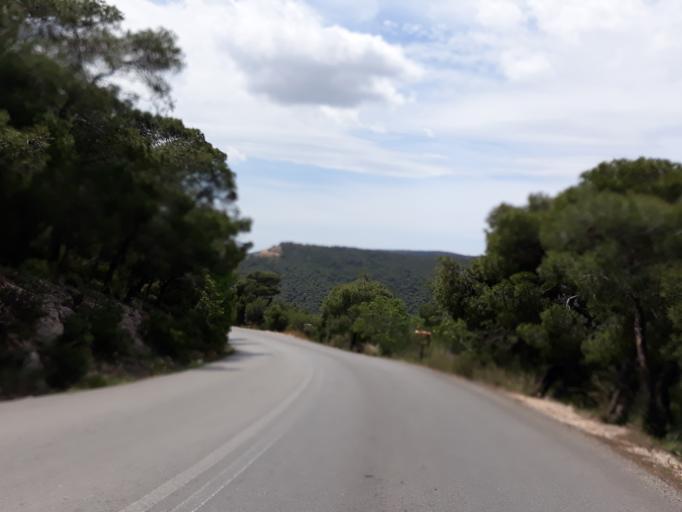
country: GR
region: Attica
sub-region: Nomarchia Dytikis Attikis
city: Magoula
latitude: 38.1489
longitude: 23.5177
